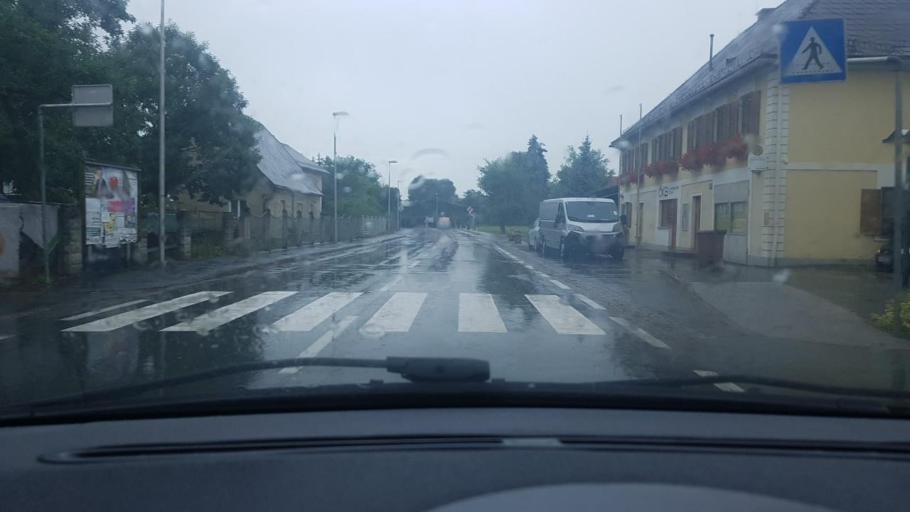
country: AT
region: Styria
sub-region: Politischer Bezirk Graz-Umgebung
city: Zettling
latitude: 46.9587
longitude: 15.4276
